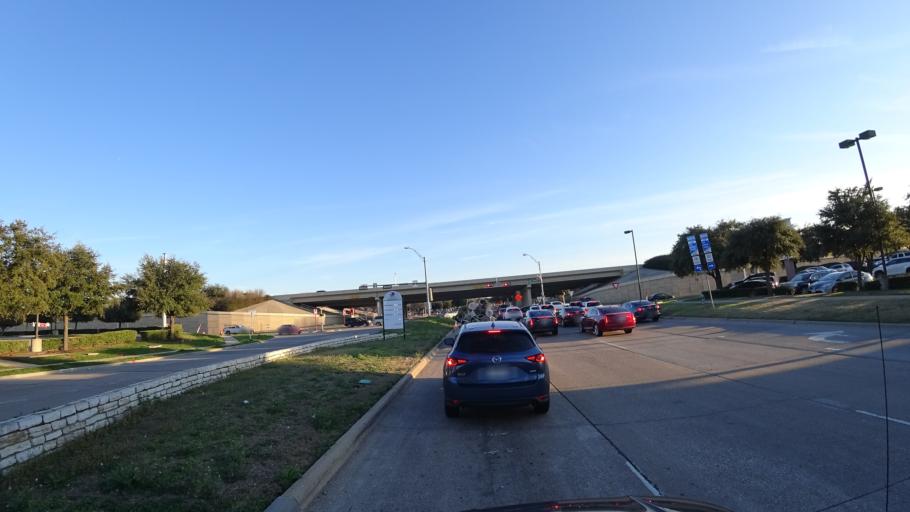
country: US
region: Texas
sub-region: Denton County
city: Lewisville
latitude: 32.9937
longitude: -96.9751
